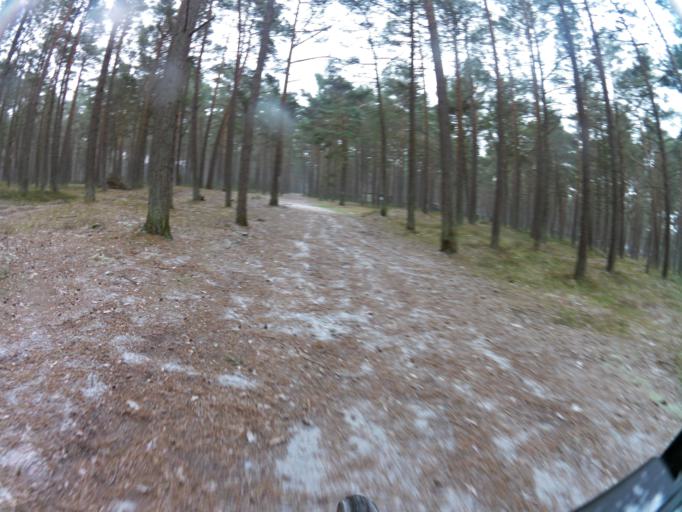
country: PL
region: West Pomeranian Voivodeship
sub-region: Powiat gryficki
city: Cerkwica
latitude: 54.1061
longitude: 15.1314
